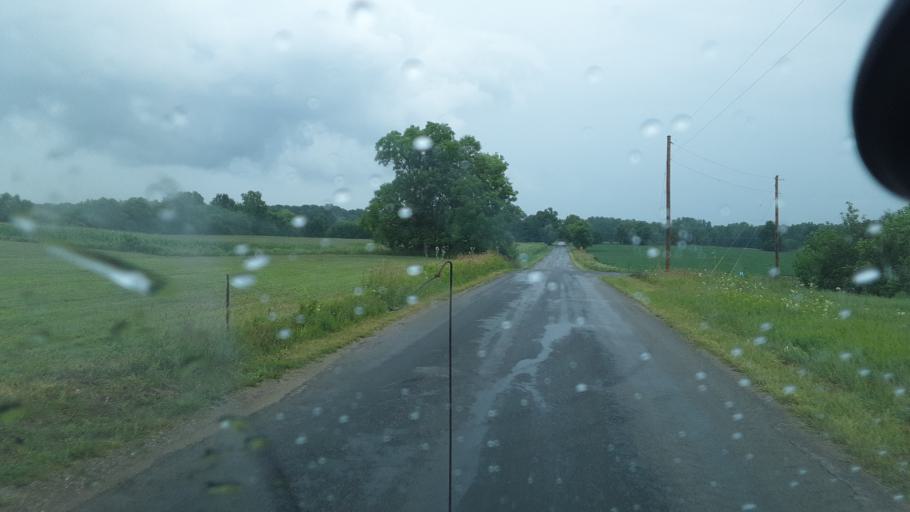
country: US
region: Indiana
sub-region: Steuben County
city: Hamilton
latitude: 41.5448
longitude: -84.8549
